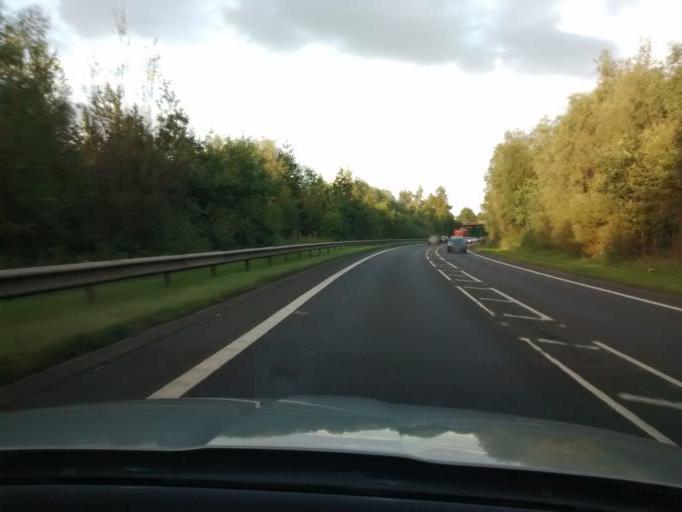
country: GB
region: Scotland
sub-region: Renfrewshire
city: Howwood
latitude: 55.8102
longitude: -4.5652
